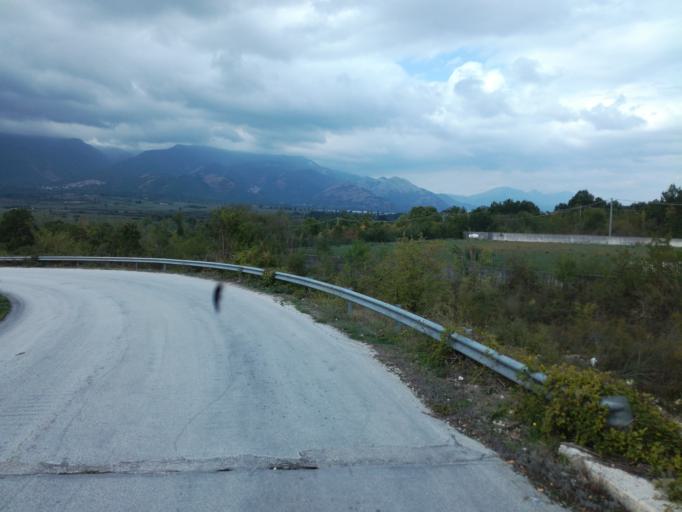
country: IT
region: Molise
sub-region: Provincia di Campobasso
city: Guardiaregia
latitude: 41.4679
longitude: 14.5589
